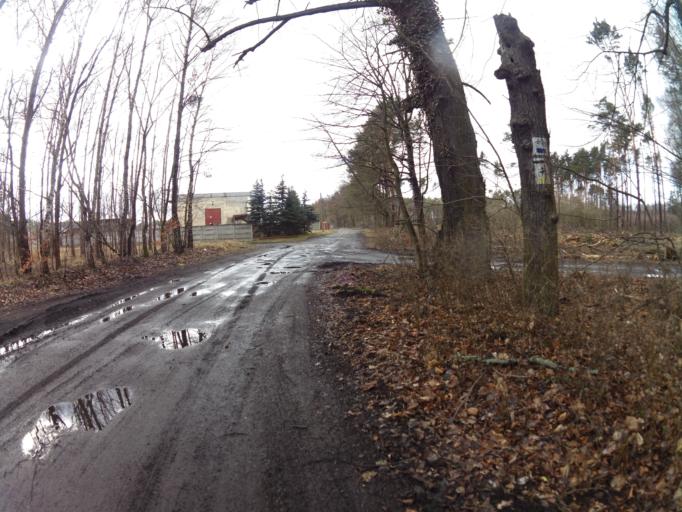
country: PL
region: West Pomeranian Voivodeship
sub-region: Powiat mysliborski
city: Debno
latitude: 52.7342
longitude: 14.7233
